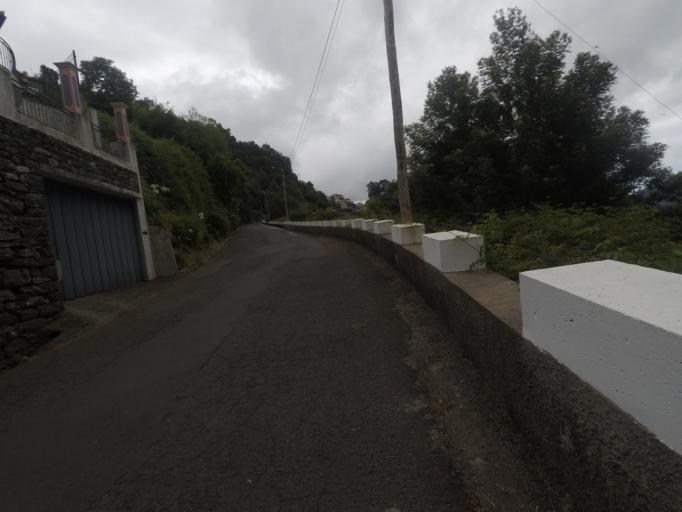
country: PT
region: Madeira
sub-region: Santana
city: Santana
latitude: 32.7563
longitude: -16.8788
